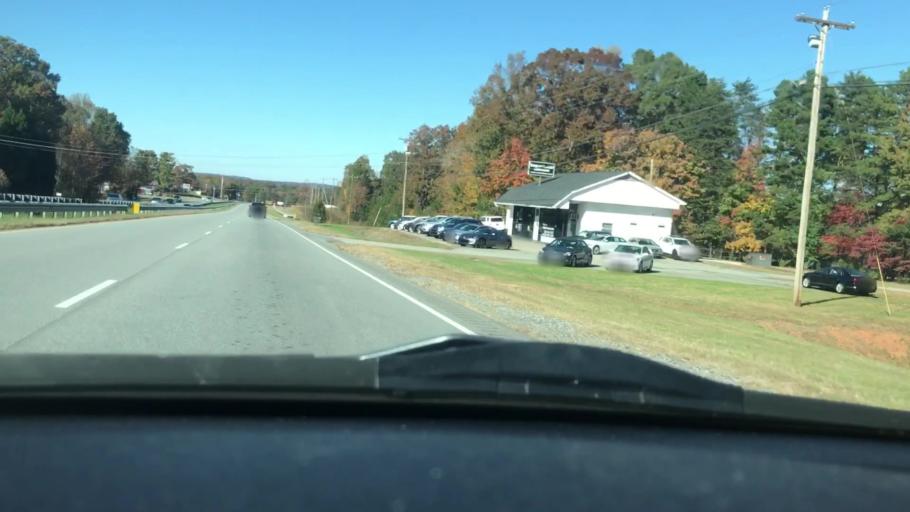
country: US
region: North Carolina
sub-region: Rockingham County
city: Madison
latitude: 36.3490
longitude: -79.9457
